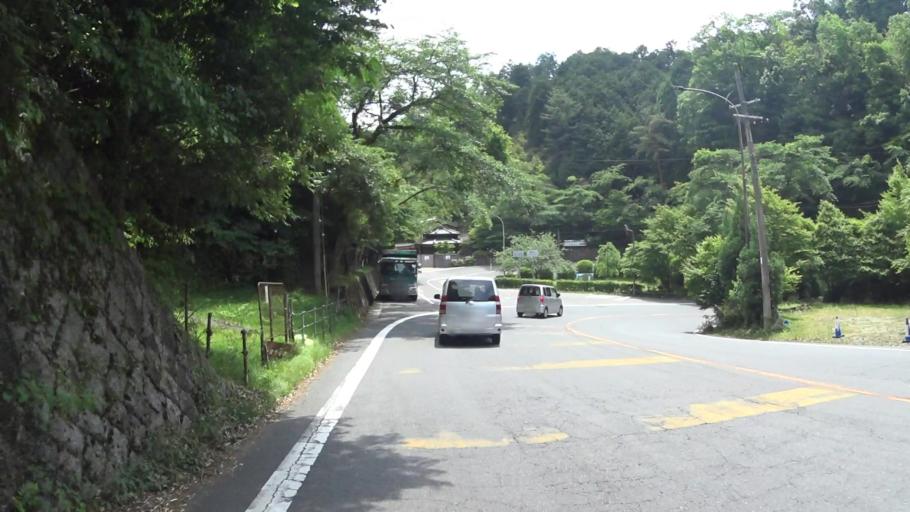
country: JP
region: Kyoto
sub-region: Kyoto-shi
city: Kamigyo-ku
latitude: 35.0536
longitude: 135.6764
